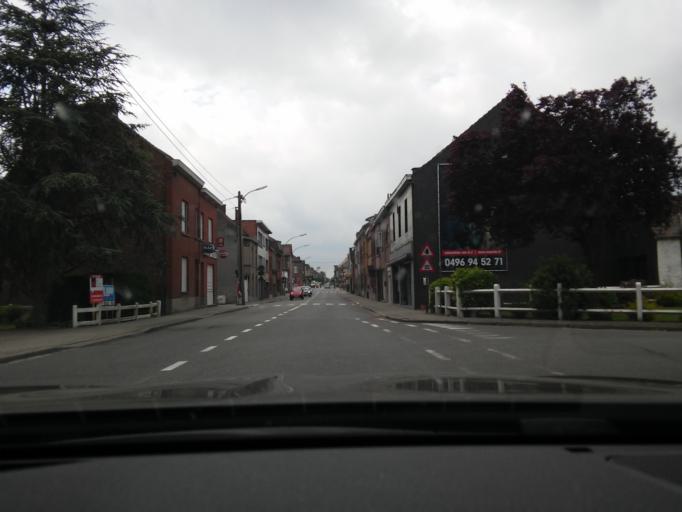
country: BE
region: Flanders
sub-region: Provincie Vlaams-Brabant
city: Ternat
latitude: 50.8761
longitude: 4.1639
